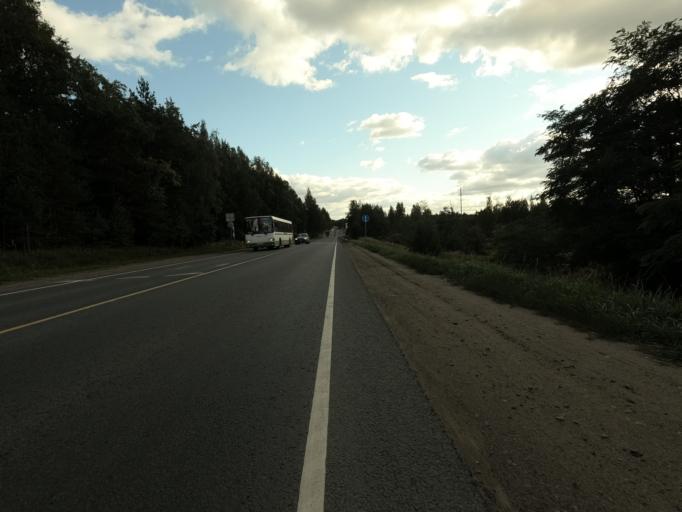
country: RU
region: Leningrad
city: Vsevolozhsk
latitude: 59.9799
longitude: 30.6540
